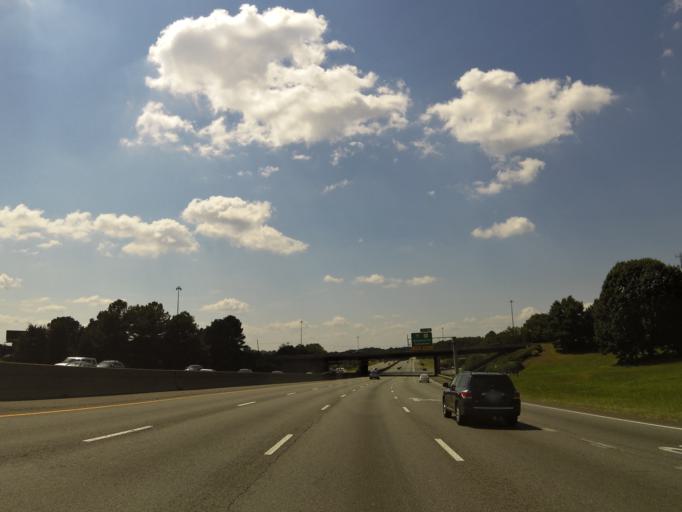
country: US
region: North Carolina
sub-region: Mecklenburg County
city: Charlotte
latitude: 35.2729
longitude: -80.8345
